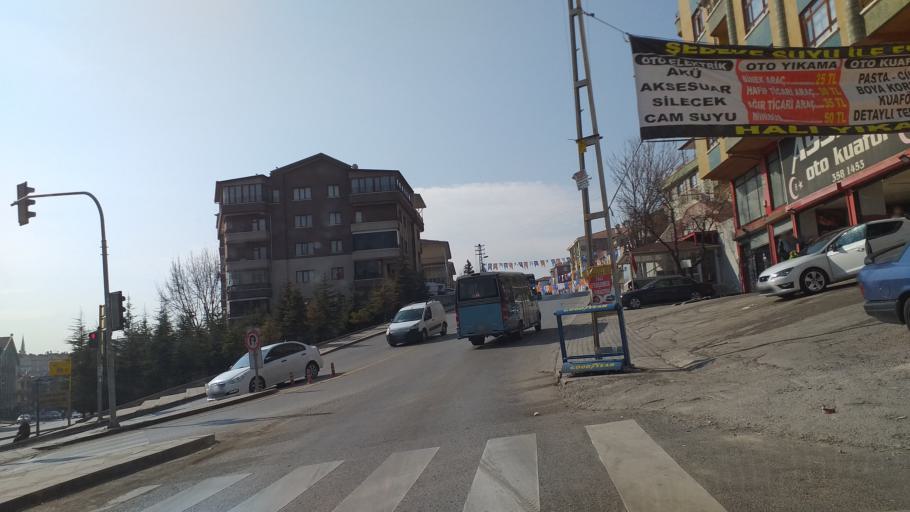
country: TR
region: Ankara
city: Ankara
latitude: 39.9920
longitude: 32.8565
